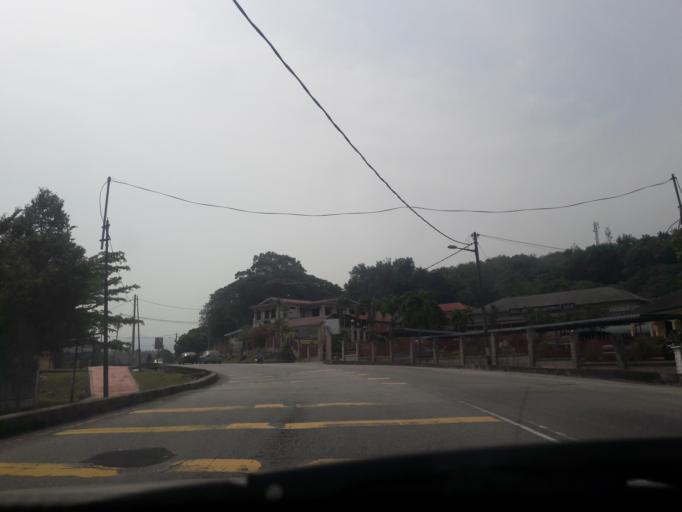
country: MY
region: Kedah
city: Kulim
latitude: 5.3683
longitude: 100.5583
